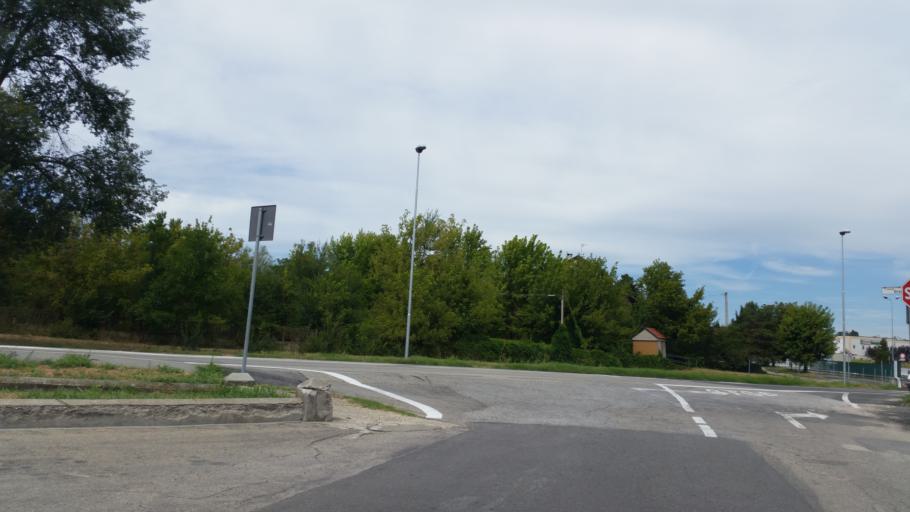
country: IT
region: Piedmont
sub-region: Provincia di Asti
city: Asti
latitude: 44.9036
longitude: 8.1752
